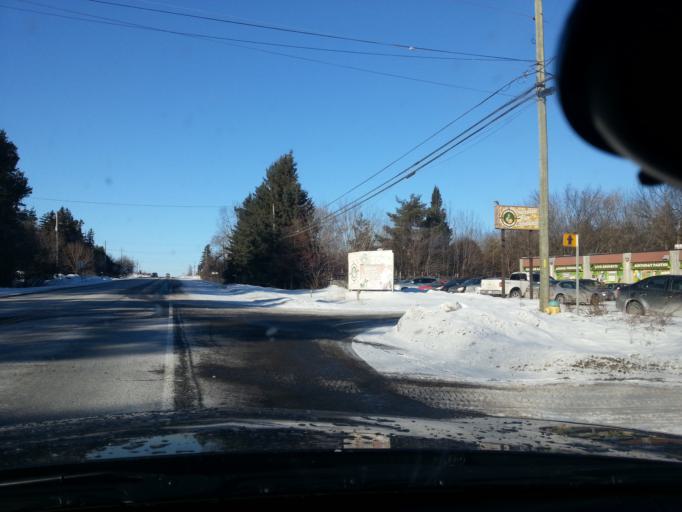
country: CA
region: Ontario
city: Ottawa
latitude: 45.2879
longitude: -75.5749
